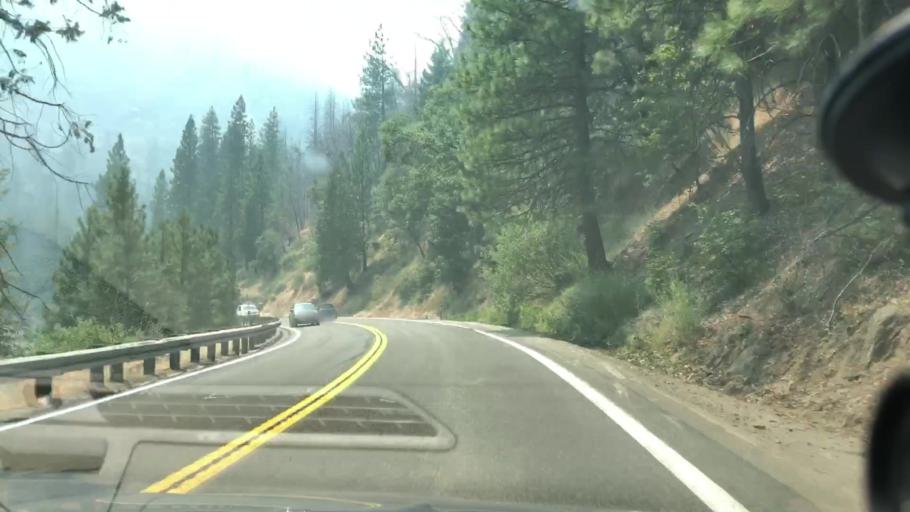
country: US
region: California
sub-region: El Dorado County
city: Pollock Pines
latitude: 38.7667
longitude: -120.3571
